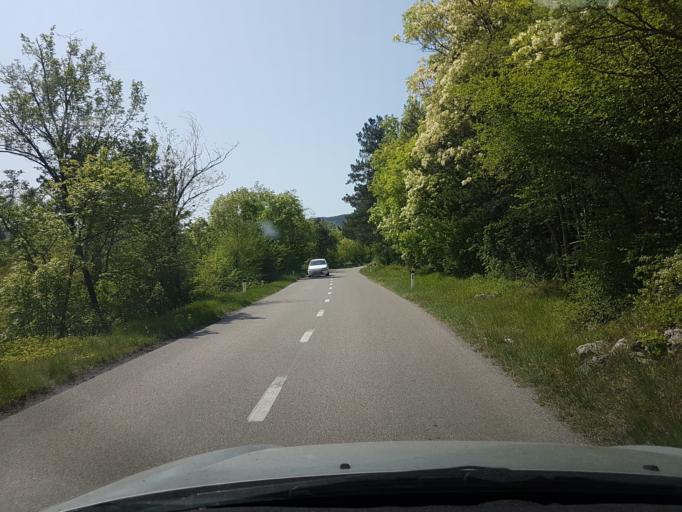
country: SI
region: Komen
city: Komen
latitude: 45.7891
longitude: 13.7063
